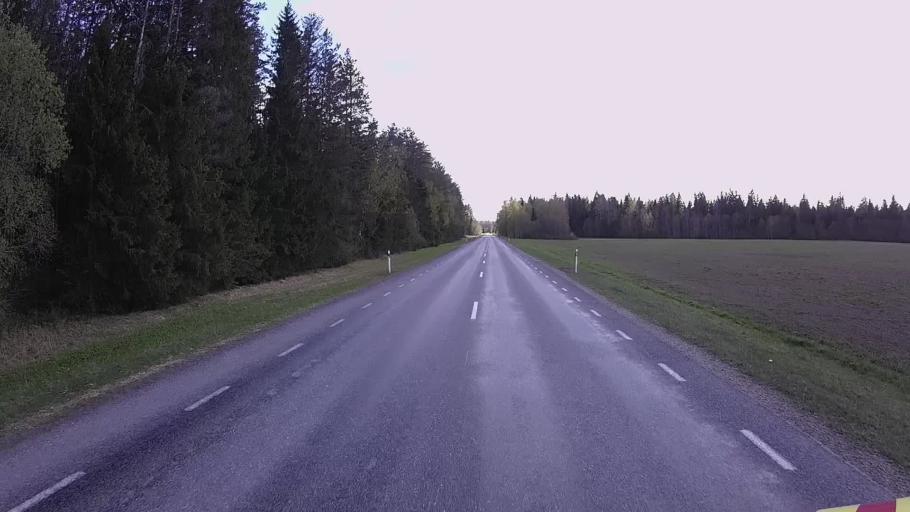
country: EE
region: Jogevamaa
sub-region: Jogeva linn
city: Jogeva
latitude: 58.7464
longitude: 26.3087
